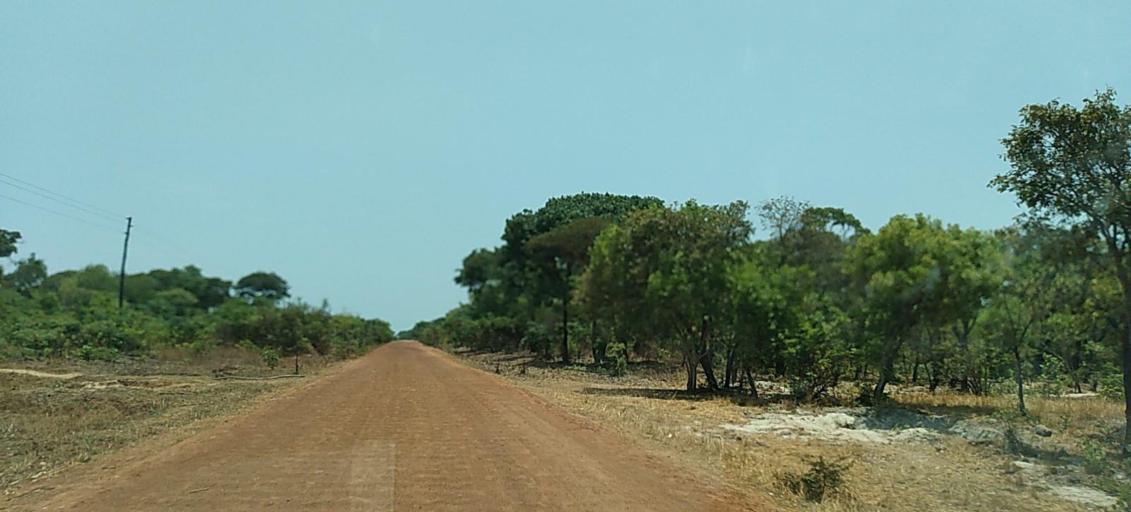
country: ZM
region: Copperbelt
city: Mpongwe
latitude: -13.7955
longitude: 27.8616
